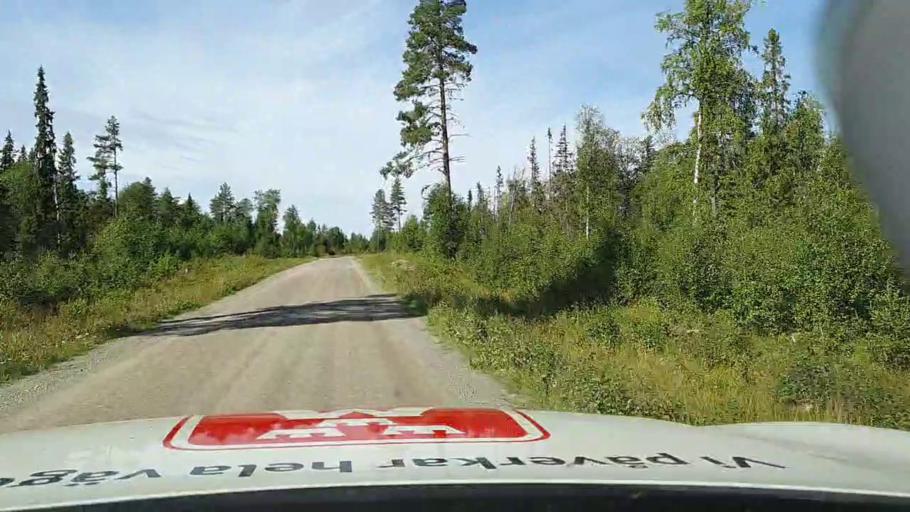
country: SE
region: Jaemtland
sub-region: Stroemsunds Kommun
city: Stroemsund
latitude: 63.7116
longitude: 15.3059
